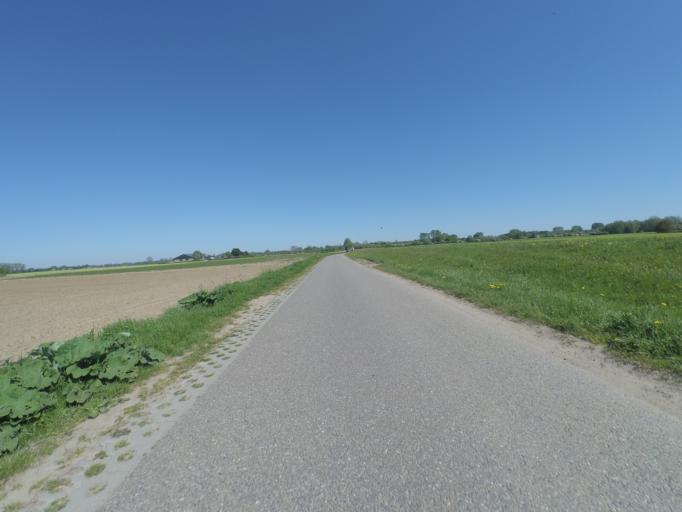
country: NL
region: Gelderland
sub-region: Gemeente Lochem
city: Gorssel
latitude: 52.2105
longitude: 6.1804
